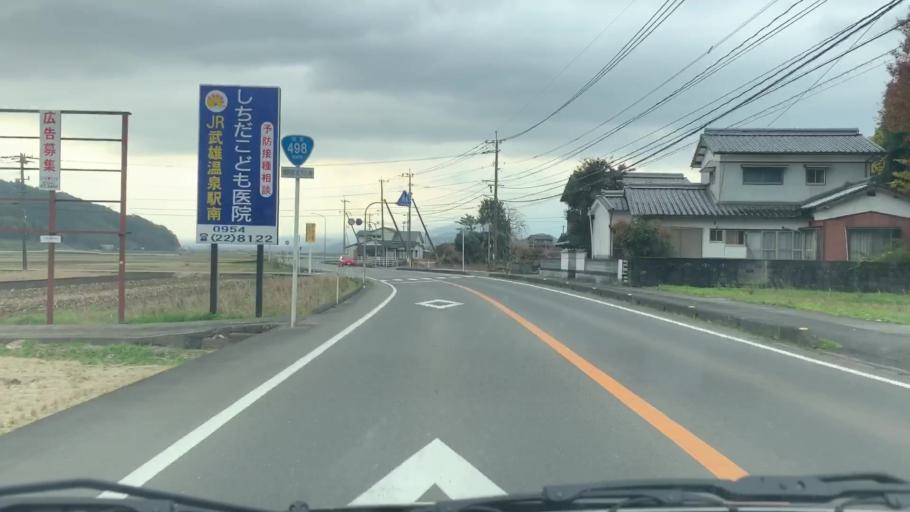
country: JP
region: Saga Prefecture
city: Kashima
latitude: 33.1452
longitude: 130.0633
